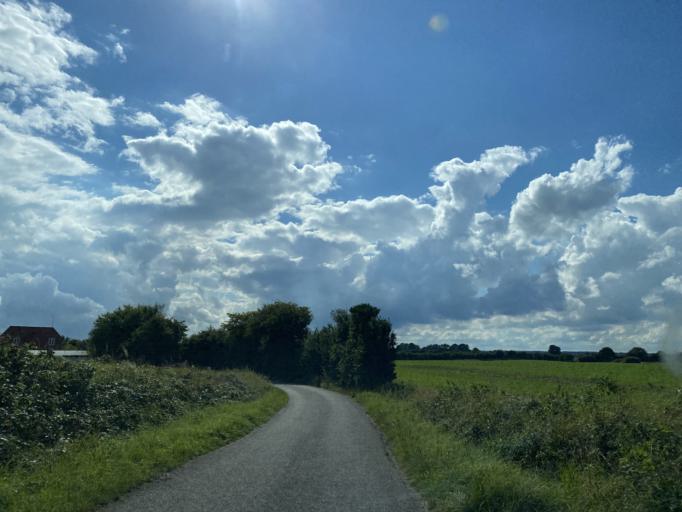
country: DK
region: South Denmark
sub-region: Haderslev Kommune
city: Starup
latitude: 55.1856
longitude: 9.5072
